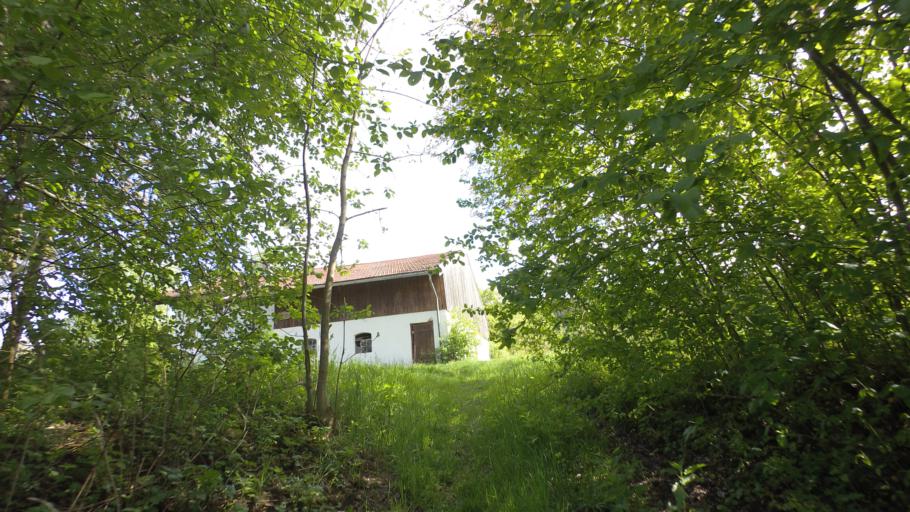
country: DE
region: Bavaria
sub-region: Upper Bavaria
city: Grabenstatt
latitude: 47.8450
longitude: 12.5710
